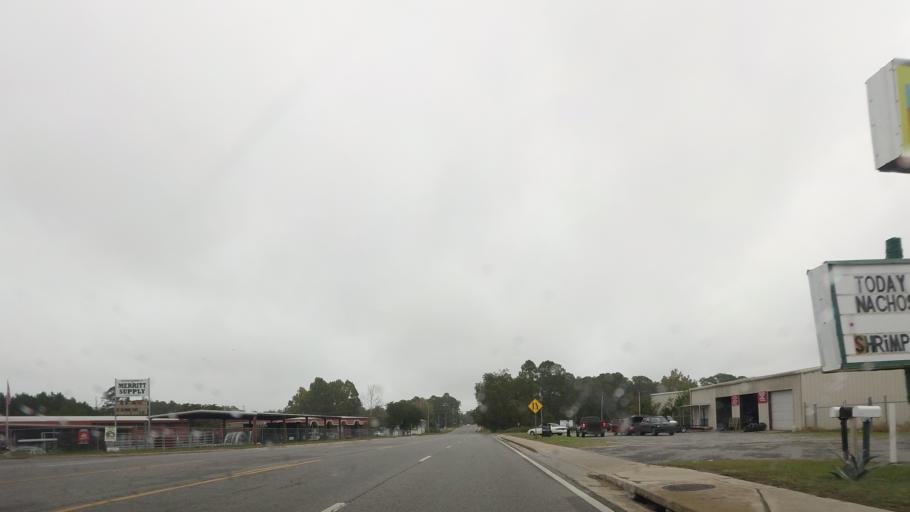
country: US
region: Georgia
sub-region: Ben Hill County
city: Fitzgerald
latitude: 31.7260
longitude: -83.2516
